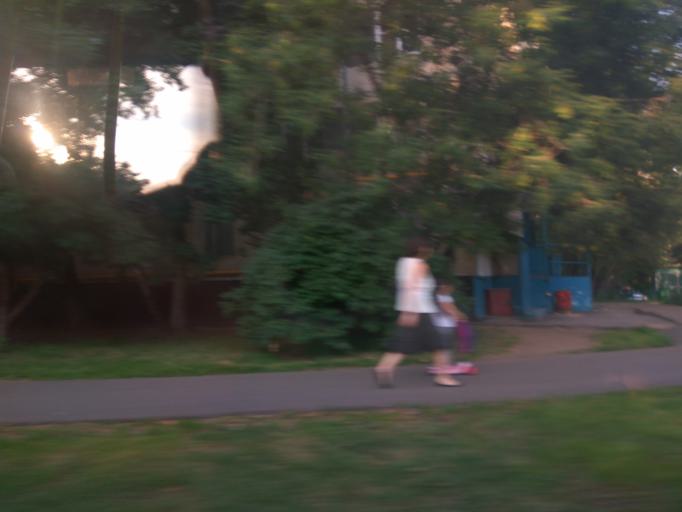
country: RU
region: Moskovskaya
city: Biryulevo Zapadnoye
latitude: 55.6009
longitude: 37.6219
